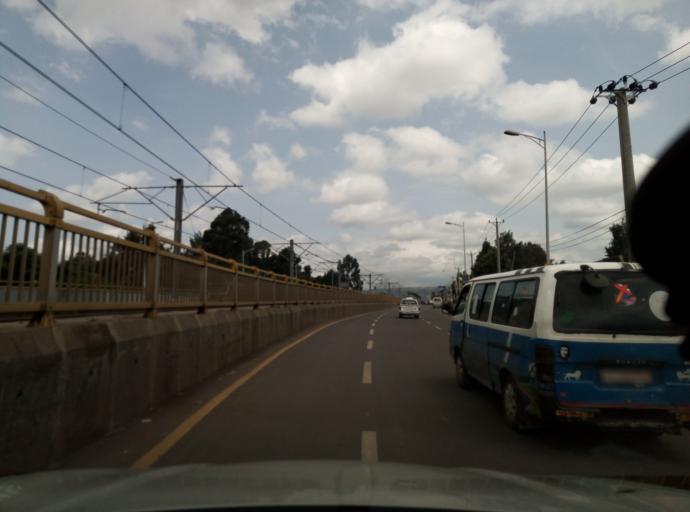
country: ET
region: Adis Abeba
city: Addis Ababa
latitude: 9.0108
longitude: 38.7245
